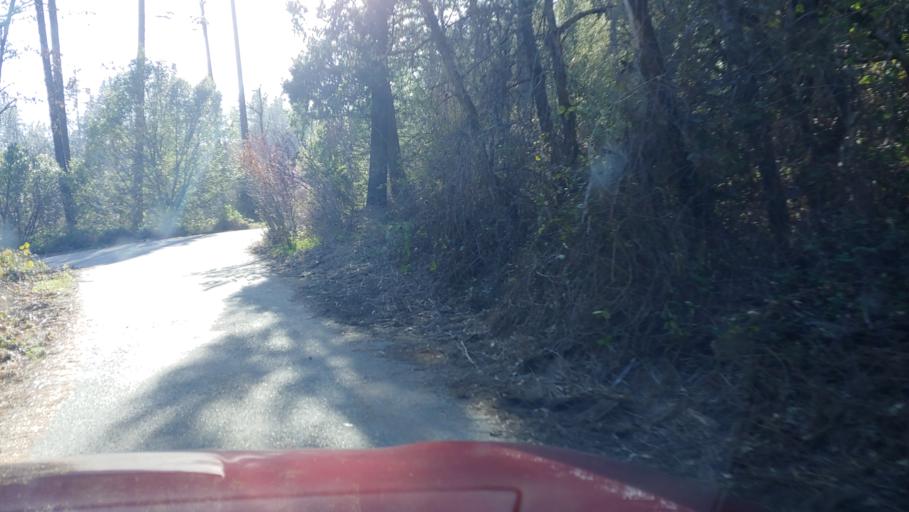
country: US
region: California
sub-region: Siskiyou County
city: Dunsmuir
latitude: 40.9967
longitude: -122.4129
